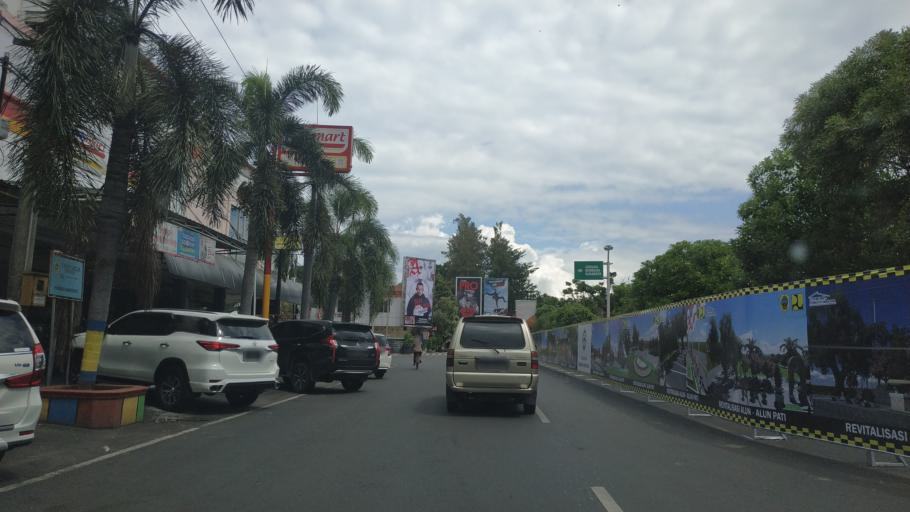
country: ID
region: Central Java
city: Pati
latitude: -6.7530
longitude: 111.0405
